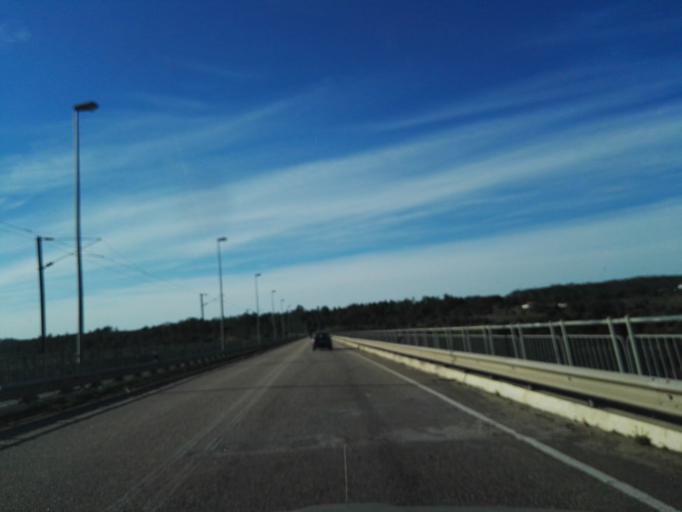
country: PT
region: Santarem
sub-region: Abrantes
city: Alferrarede
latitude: 39.4700
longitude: -8.0629
